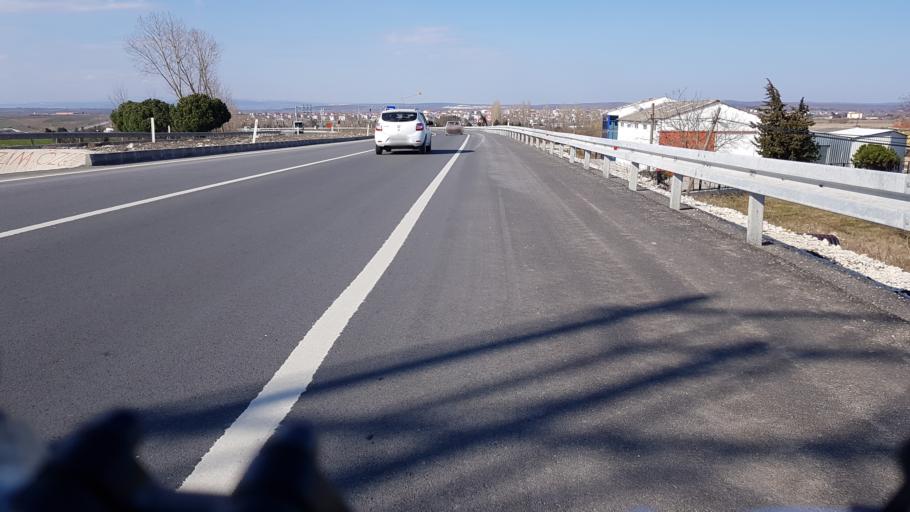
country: TR
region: Tekirdag
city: Saray
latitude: 41.4157
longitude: 27.9224
